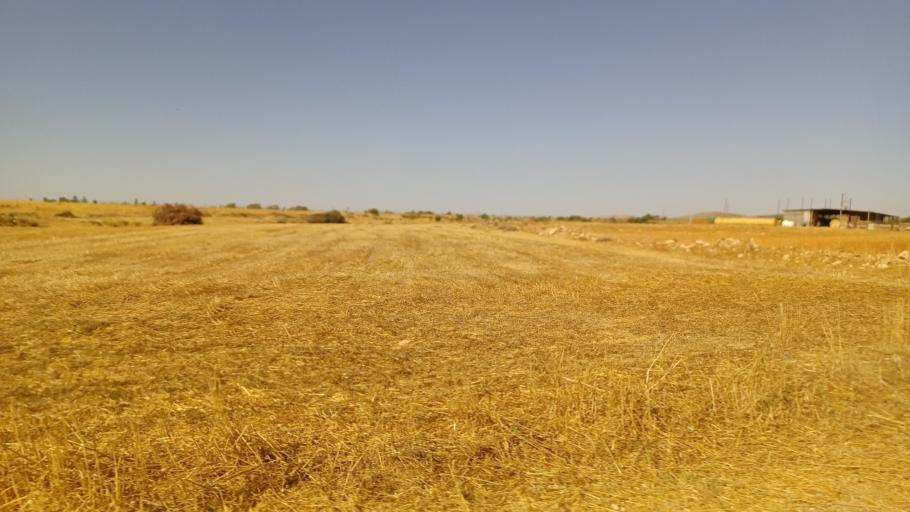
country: CY
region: Larnaka
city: Pergamos
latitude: 35.0527
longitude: 33.7003
